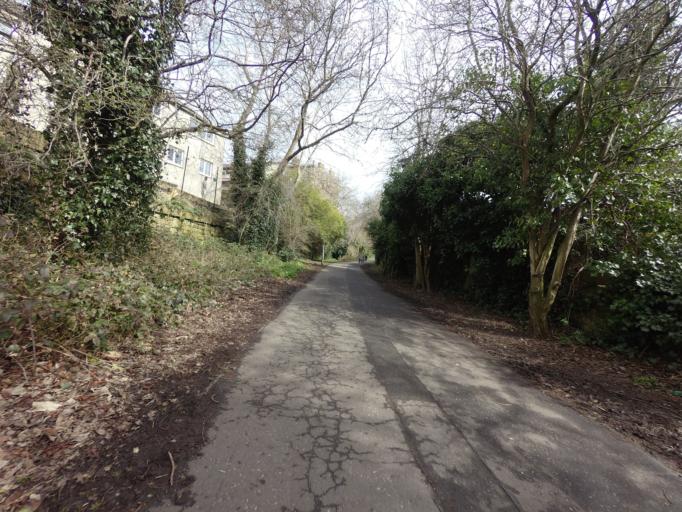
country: GB
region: Scotland
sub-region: Edinburgh
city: Edinburgh
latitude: 55.9717
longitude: -3.1901
